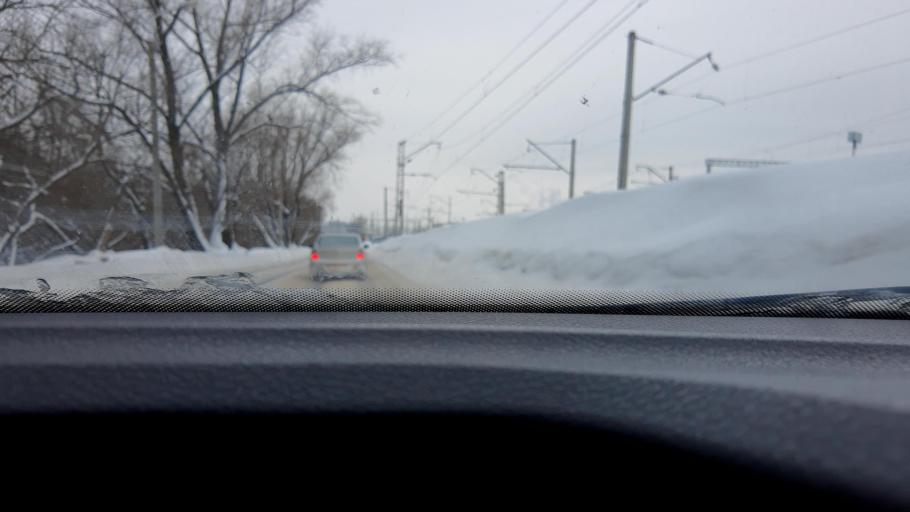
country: RU
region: Bashkortostan
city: Mikhaylovka
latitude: 54.7017
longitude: 55.8548
